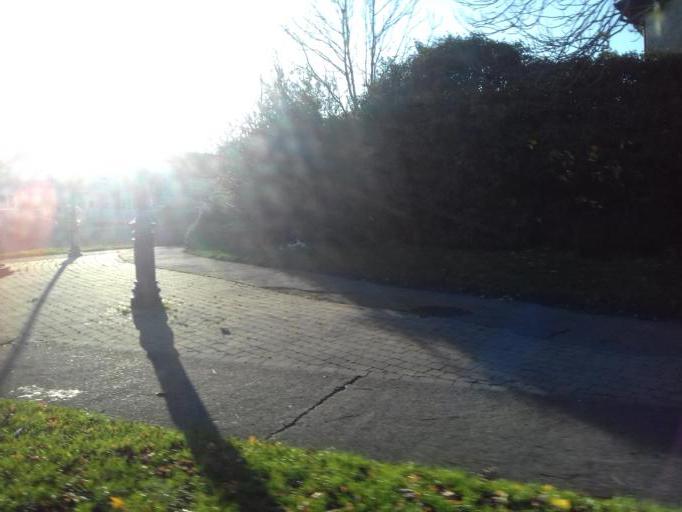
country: IE
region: Leinster
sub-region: Dublin City
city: Finglas
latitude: 53.3804
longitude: -6.2974
